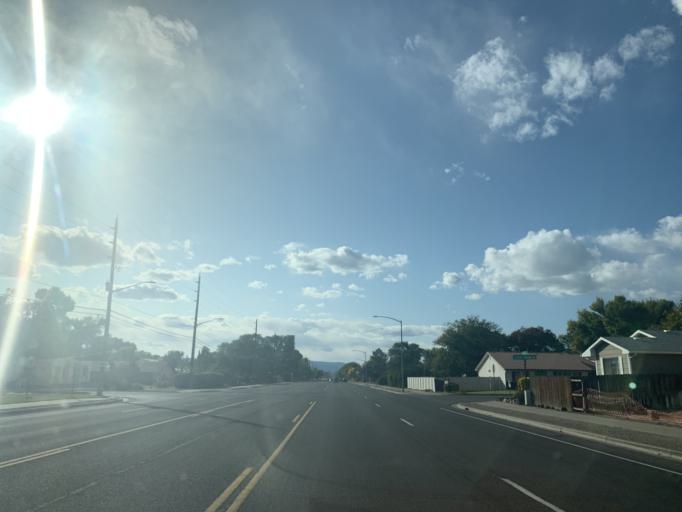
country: US
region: Colorado
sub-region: Mesa County
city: Fruitvale
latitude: 39.0918
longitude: -108.4886
